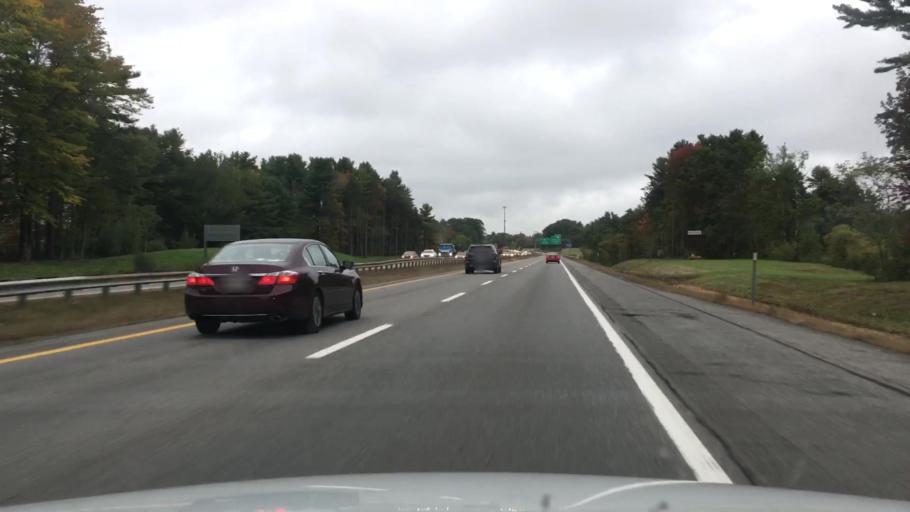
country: US
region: Maine
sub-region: Cumberland County
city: Westbrook
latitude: 43.7071
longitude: -70.3108
